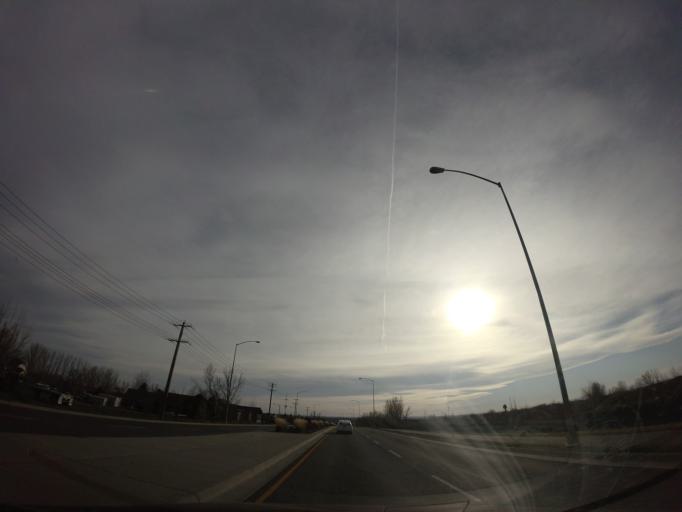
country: US
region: Montana
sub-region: Yellowstone County
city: Billings
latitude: 45.7439
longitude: -108.6175
